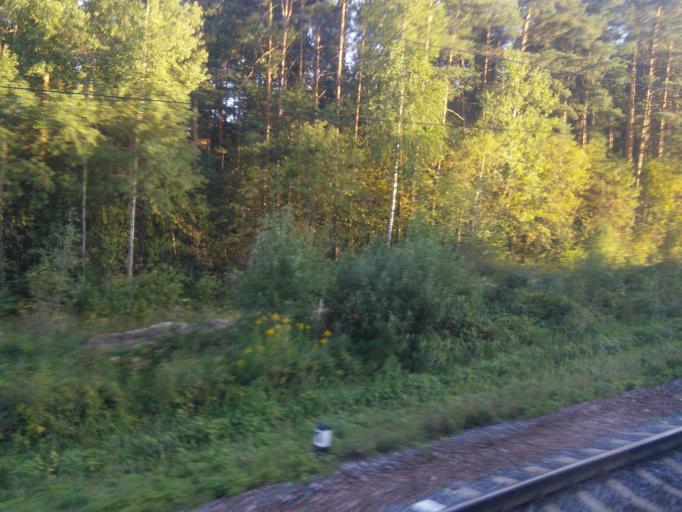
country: RU
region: Moskovskaya
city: Rakhmanovo
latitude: 55.7644
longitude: 38.6069
